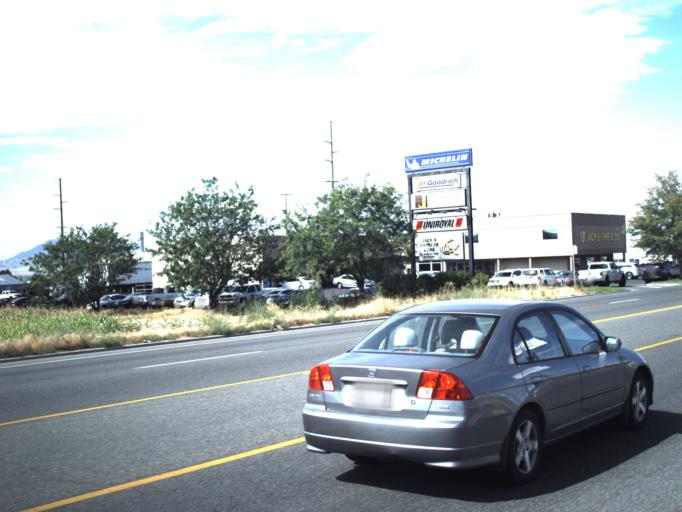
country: US
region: Utah
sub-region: Cache County
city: Logan
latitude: 41.7638
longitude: -111.8342
